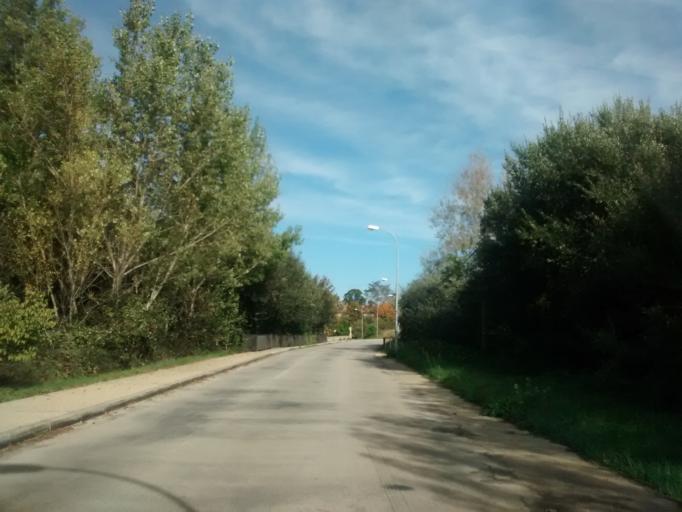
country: ES
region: Castille and Leon
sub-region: Provincia de Burgos
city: Arija
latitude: 42.9909
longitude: -3.9491
